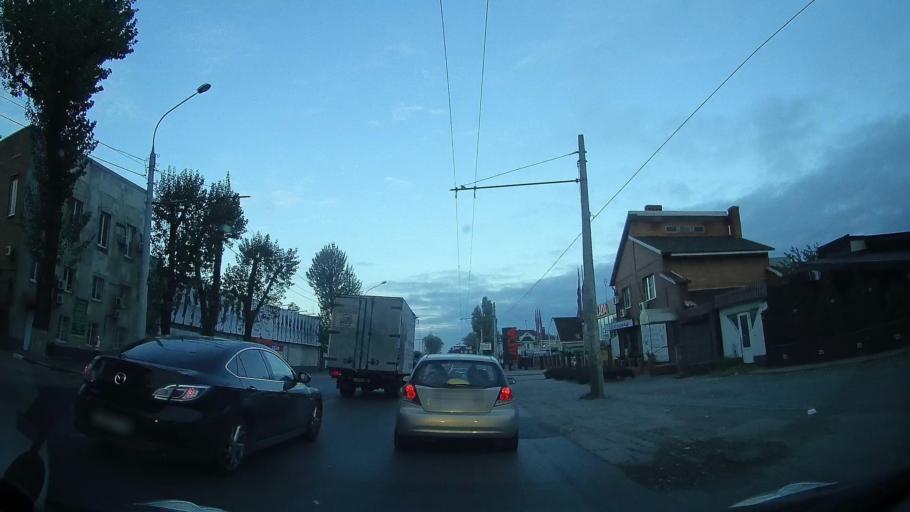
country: RU
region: Rostov
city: Severnyy
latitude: 47.2596
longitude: 39.6246
